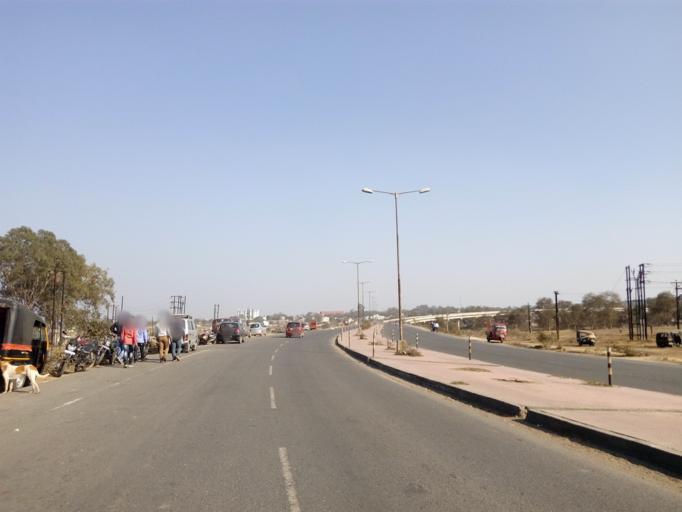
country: IN
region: Jharkhand
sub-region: Ranchi
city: Ranchi
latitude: 23.3553
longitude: 85.3666
